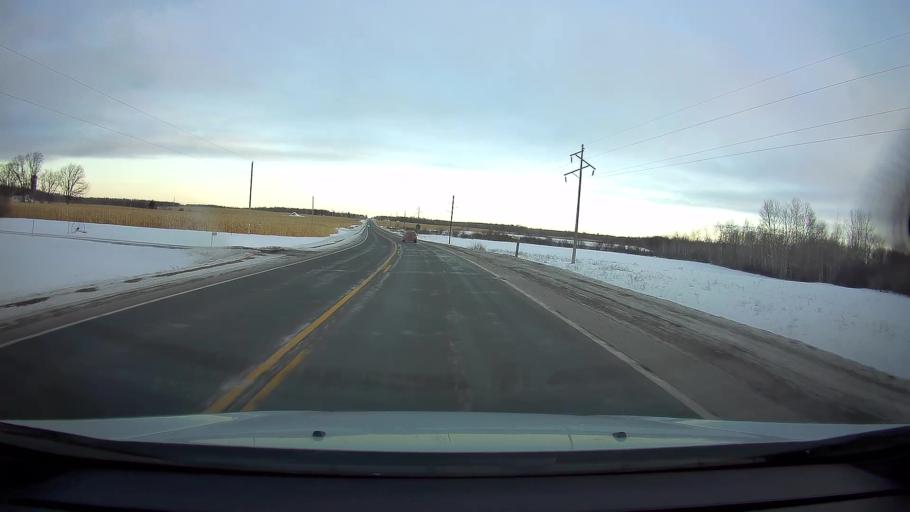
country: US
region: Wisconsin
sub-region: Barron County
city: Turtle Lake
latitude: 45.3412
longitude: -92.1669
